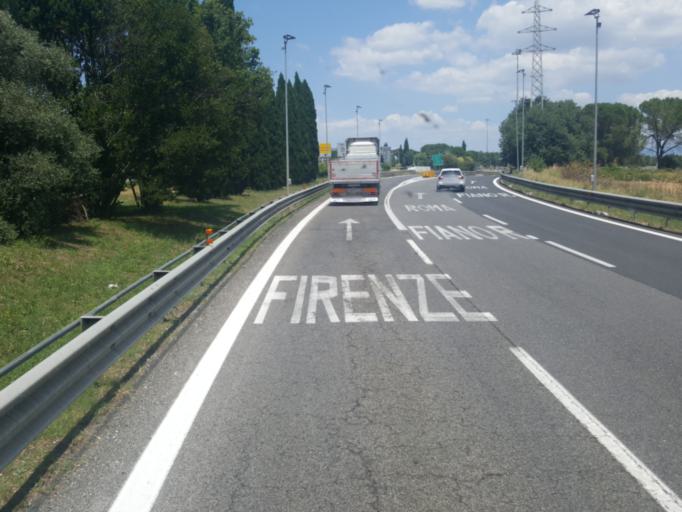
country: IT
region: Latium
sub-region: Citta metropolitana di Roma Capitale
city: Bivio di Capanelle
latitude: 42.1365
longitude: 12.6045
